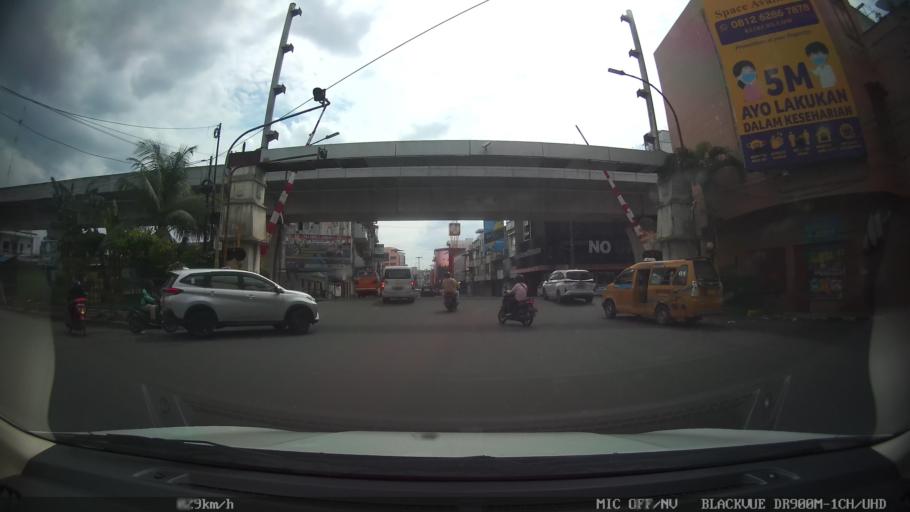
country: ID
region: North Sumatra
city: Medan
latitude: 3.5819
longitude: 98.6836
